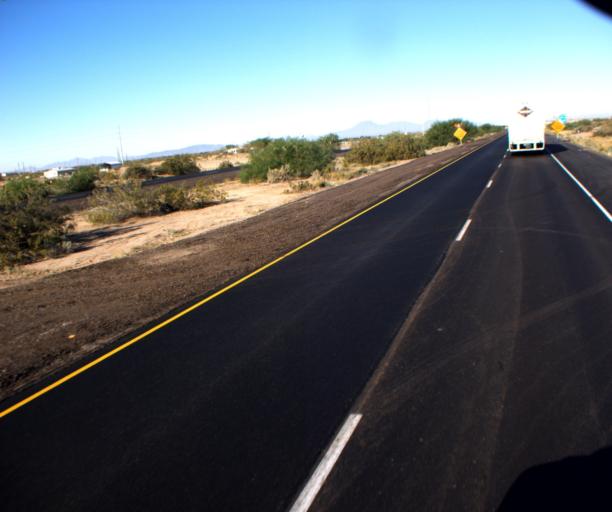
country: US
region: Arizona
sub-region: Pinal County
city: Casa Grande
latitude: 32.8282
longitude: -111.7636
